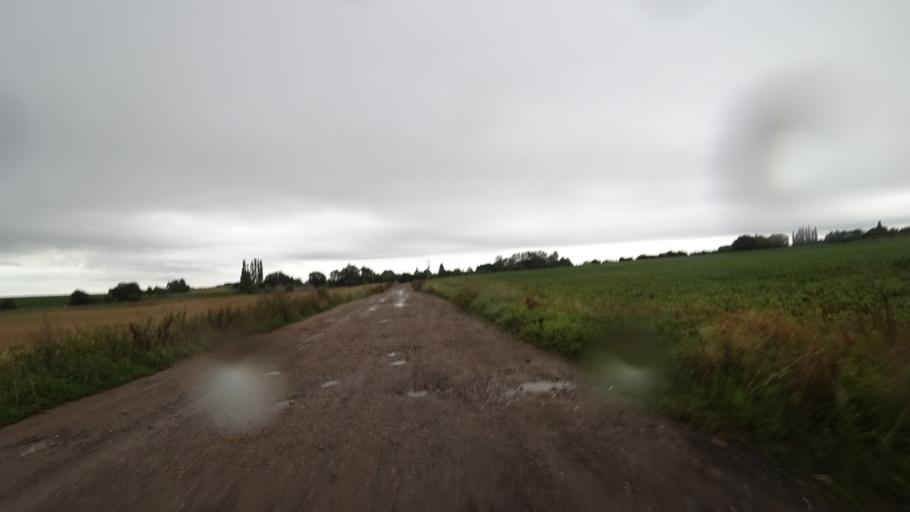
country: BE
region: Wallonia
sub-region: Province de Namur
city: Gembloux
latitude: 50.5709
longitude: 4.7323
